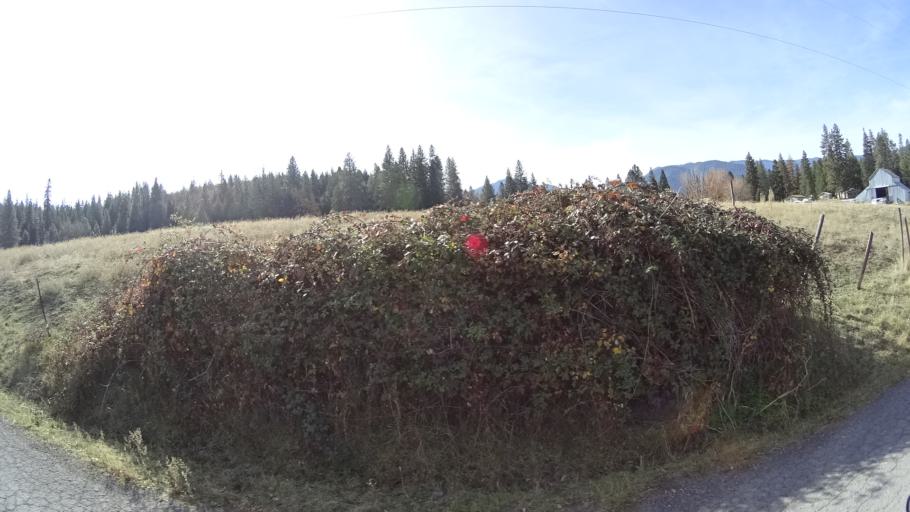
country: US
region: California
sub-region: Siskiyou County
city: Weed
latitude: 41.4333
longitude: -122.4089
